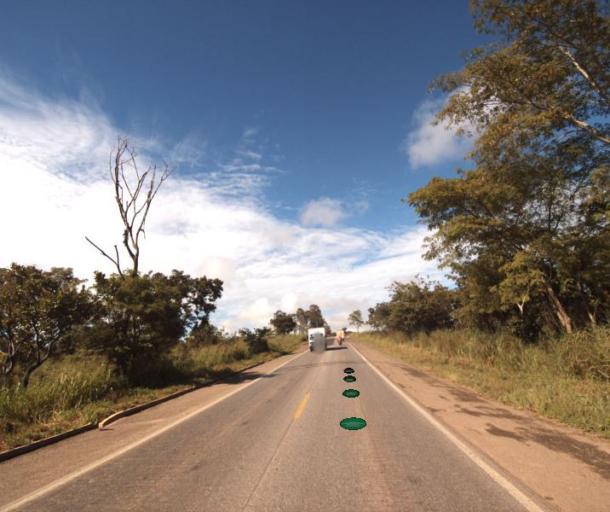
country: BR
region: Goias
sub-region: Uruacu
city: Uruacu
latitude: -14.6139
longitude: -49.1692
